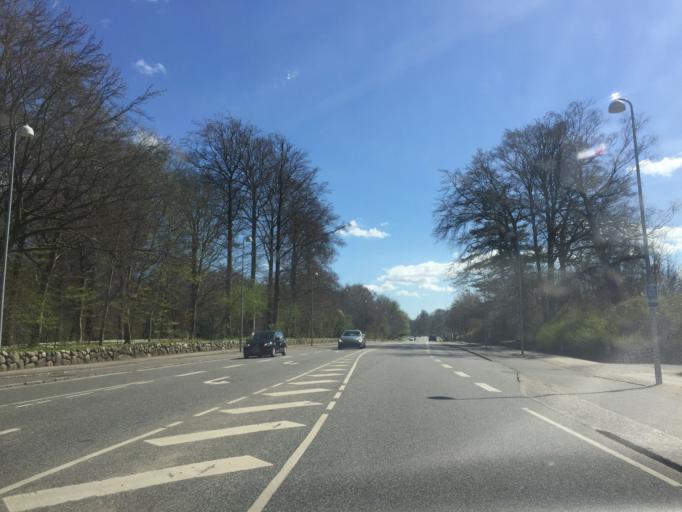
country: DK
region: Capital Region
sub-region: Lyngby-Tarbaek Kommune
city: Kongens Lyngby
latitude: 55.7837
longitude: 12.4907
